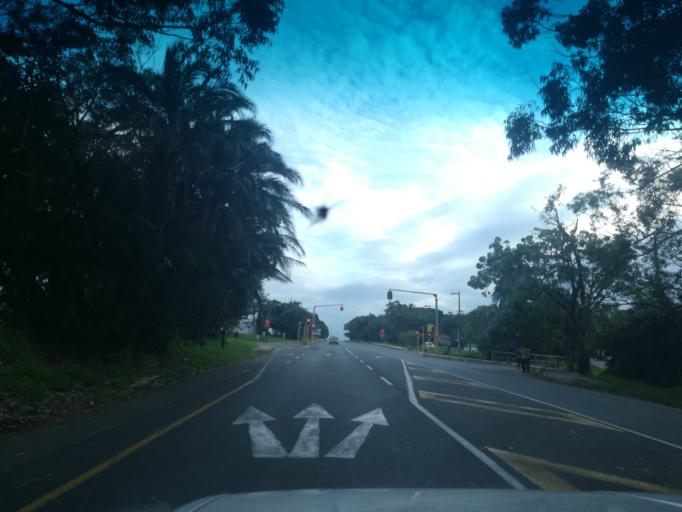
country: ZA
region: KwaZulu-Natal
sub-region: Ugu District Municipality
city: Scottburgh
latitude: -30.2952
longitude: 30.7412
